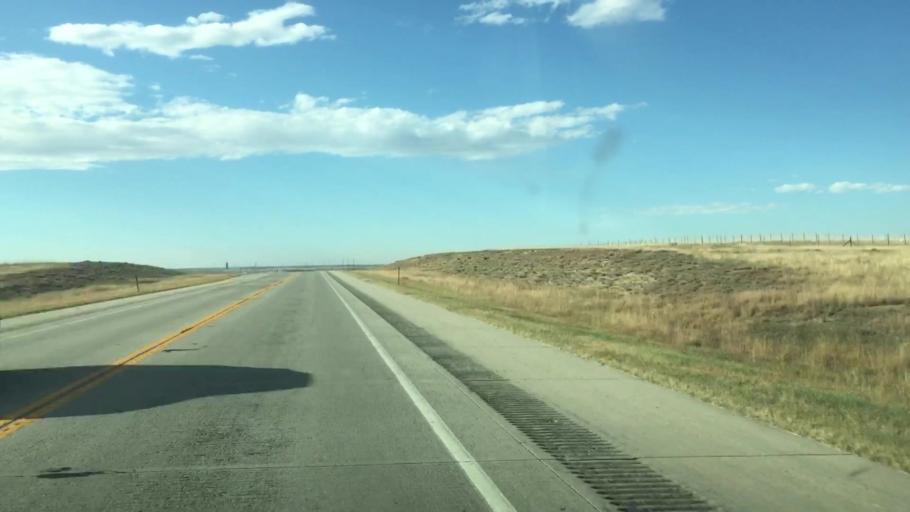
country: US
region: Colorado
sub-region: Lincoln County
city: Limon
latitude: 39.2507
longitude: -103.6347
